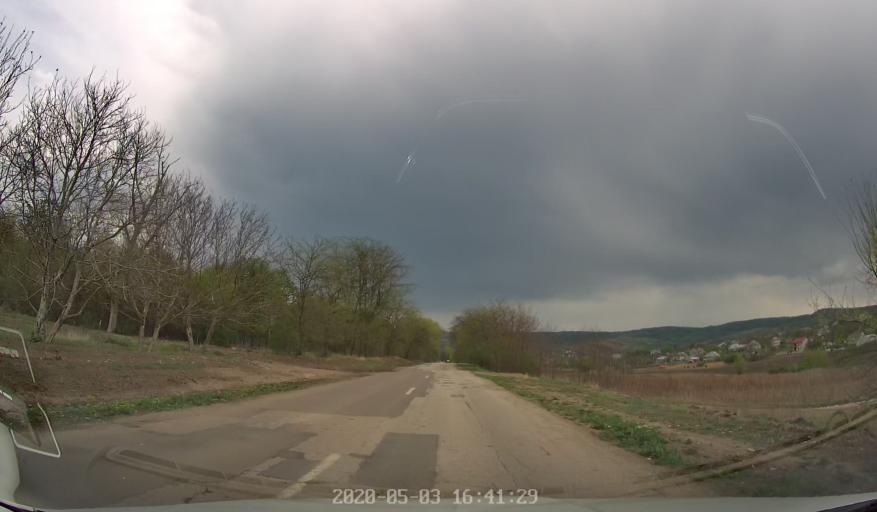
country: MD
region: Stinga Nistrului
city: Bucovat
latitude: 47.1666
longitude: 28.4087
